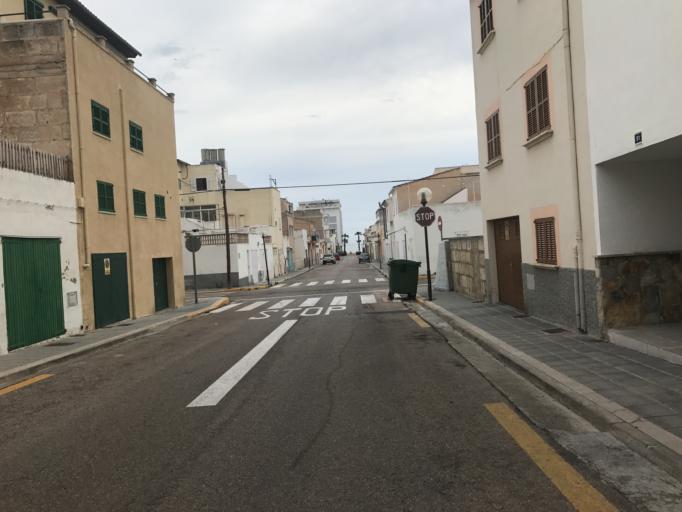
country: ES
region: Balearic Islands
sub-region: Illes Balears
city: Port d'Alcudia
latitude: 39.7642
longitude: 3.1542
